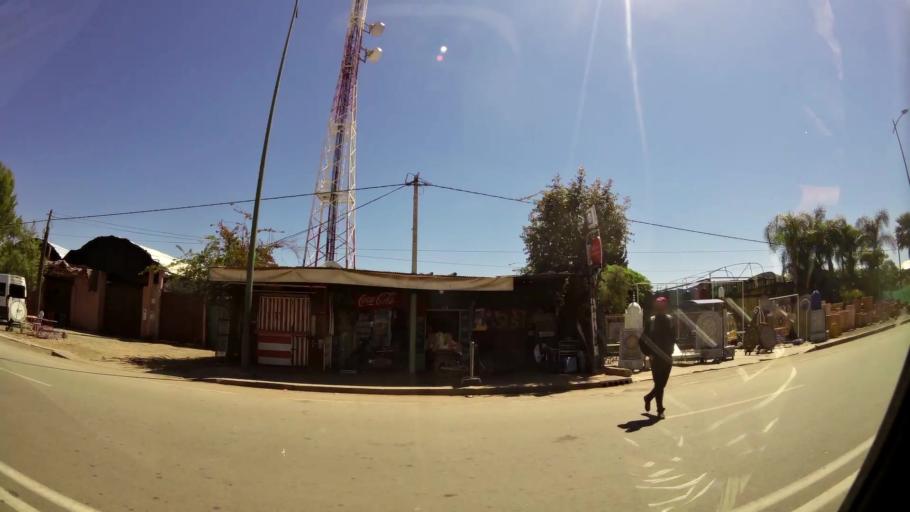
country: MA
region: Marrakech-Tensift-Al Haouz
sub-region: Marrakech
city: Marrakesh
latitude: 31.5709
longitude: -7.9806
